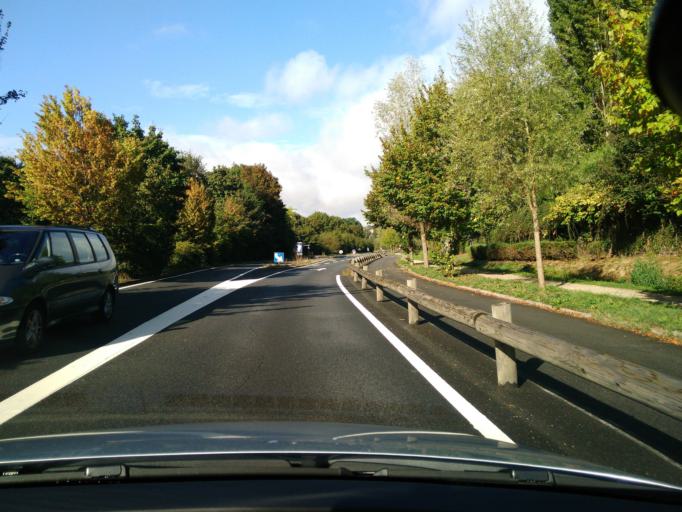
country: FR
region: Ile-de-France
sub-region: Departement de l'Essonne
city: Verrieres-le-Buisson
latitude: 48.7374
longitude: 2.2582
